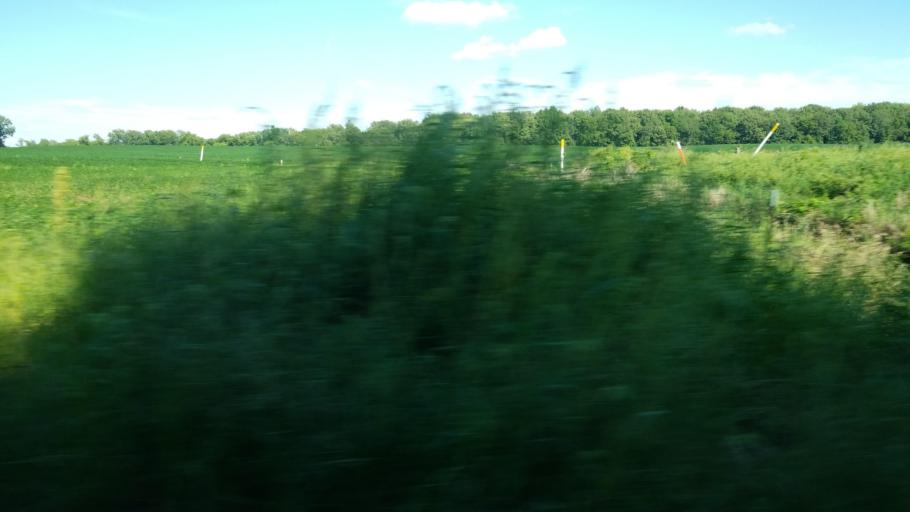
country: US
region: Illinois
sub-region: Saline County
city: Harrisburg
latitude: 37.8200
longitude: -88.5672
